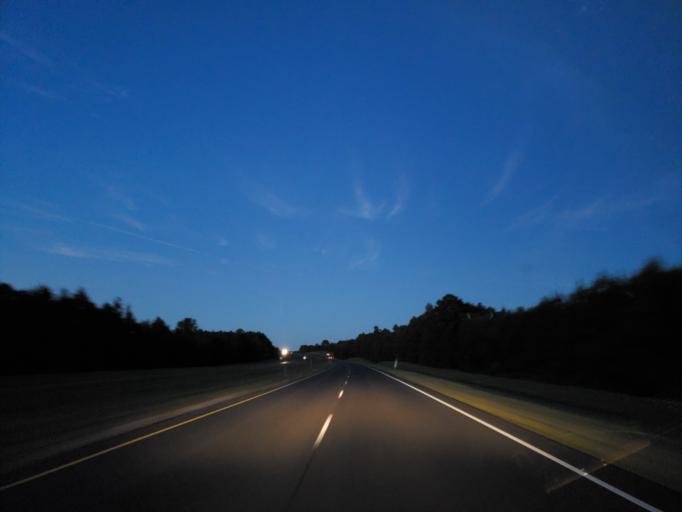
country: US
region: Mississippi
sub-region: Clarke County
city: Quitman
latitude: 31.9993
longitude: -88.6949
